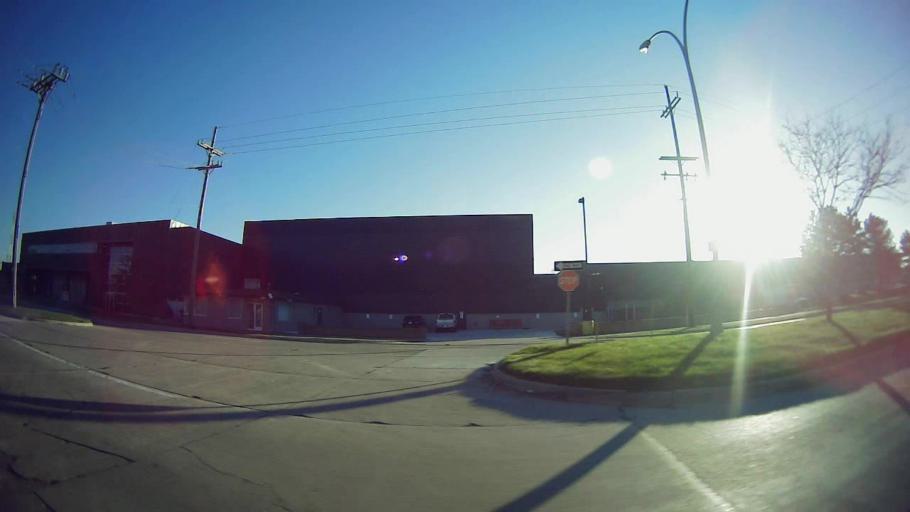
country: US
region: Michigan
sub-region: Oakland County
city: Berkley
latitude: 42.5276
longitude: -83.1844
